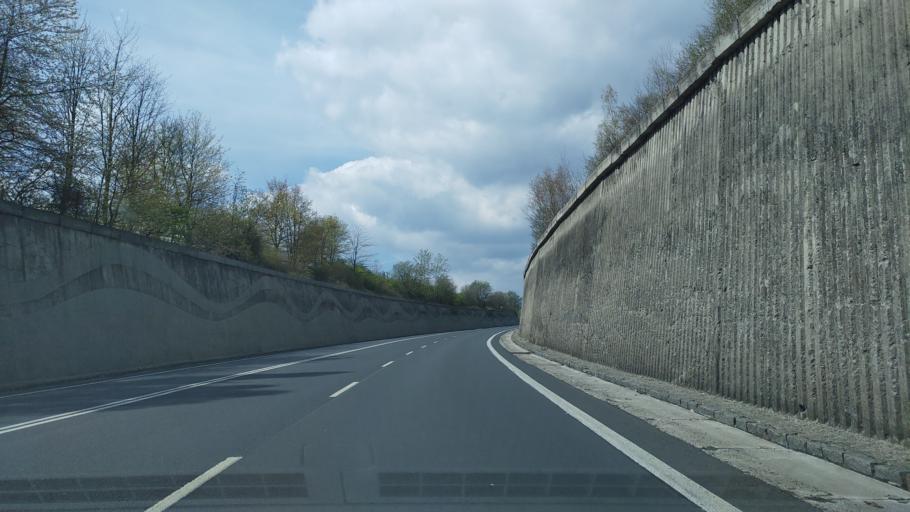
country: CZ
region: Ustecky
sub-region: Okres Chomutov
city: Klasterec nad Ohri
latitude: 50.3851
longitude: 13.1541
